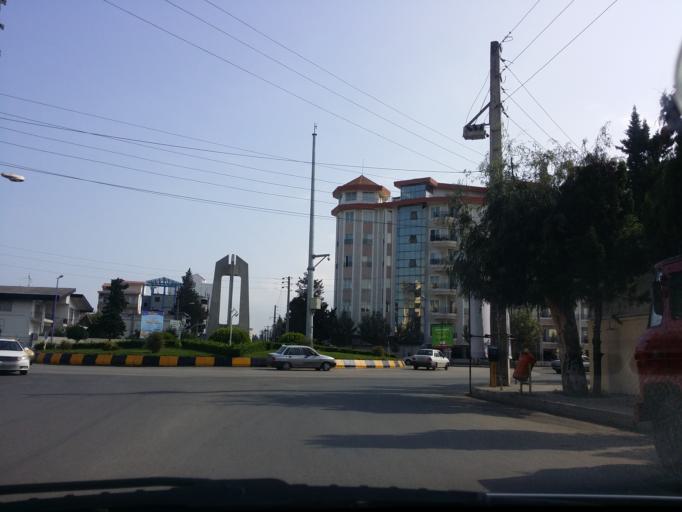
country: IR
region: Mazandaran
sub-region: Nowshahr
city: Nowshahr
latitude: 36.6478
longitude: 51.4925
